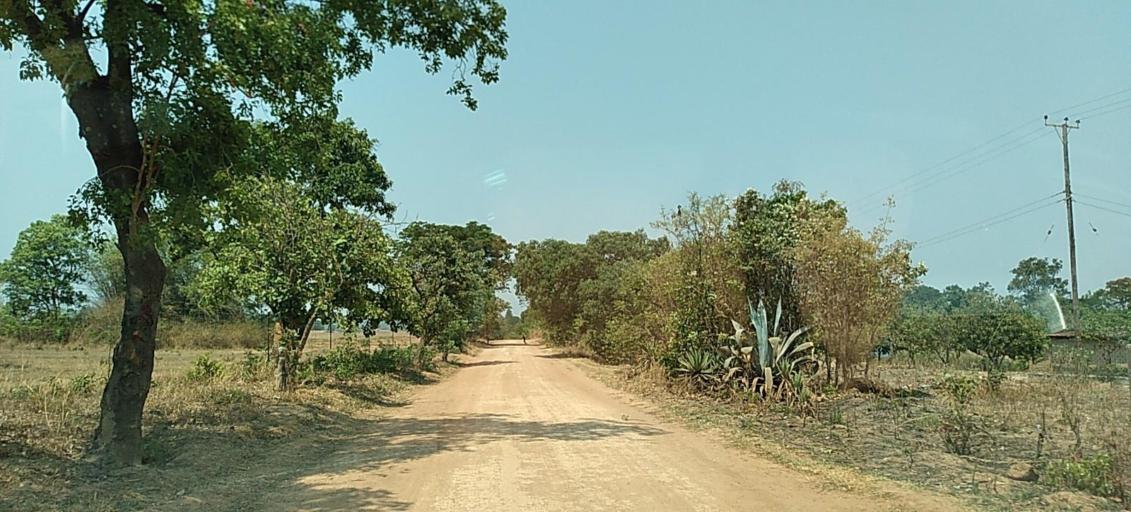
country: ZM
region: Copperbelt
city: Chambishi
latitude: -12.6214
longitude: 27.9546
